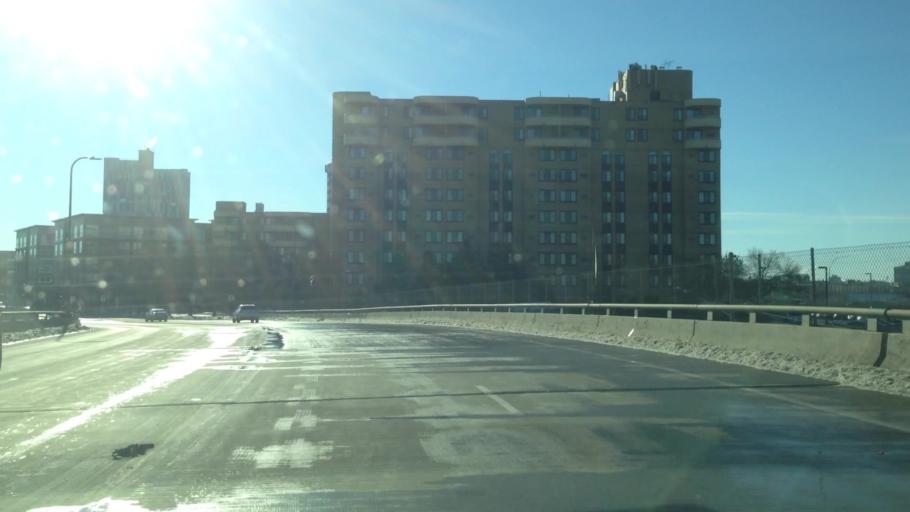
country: US
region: Minnesota
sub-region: Hennepin County
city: Minneapolis
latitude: 44.9759
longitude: -93.2456
